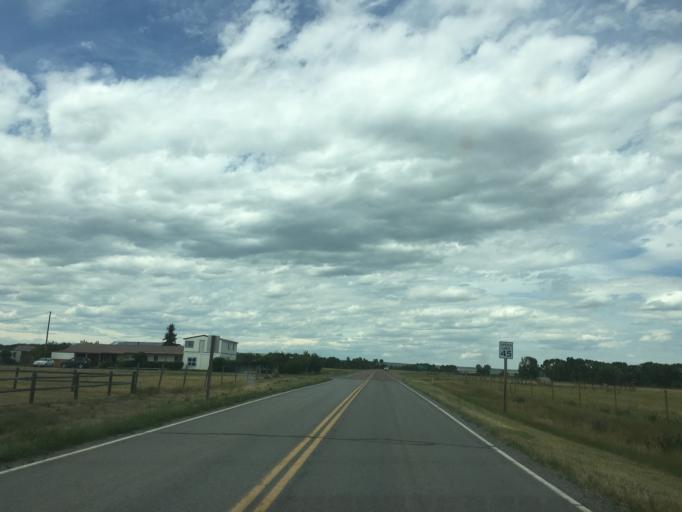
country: US
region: Montana
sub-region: Teton County
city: Choteau
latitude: 47.9798
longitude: -112.3134
